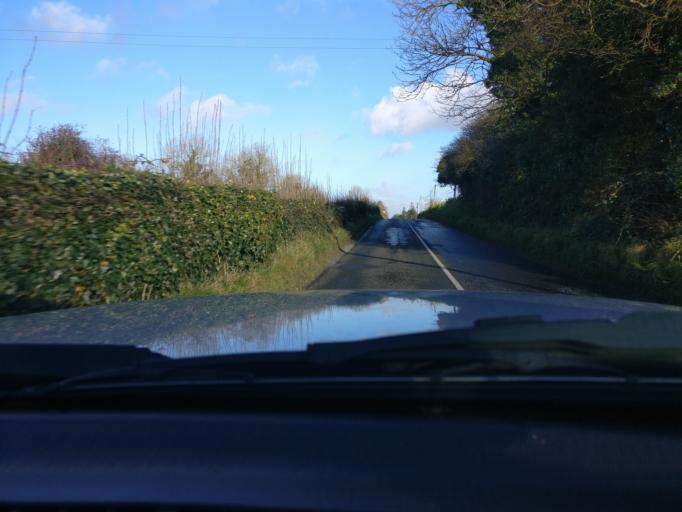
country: IE
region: Leinster
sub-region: An Iarmhi
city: Kilbeggan
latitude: 53.4535
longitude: -7.5245
